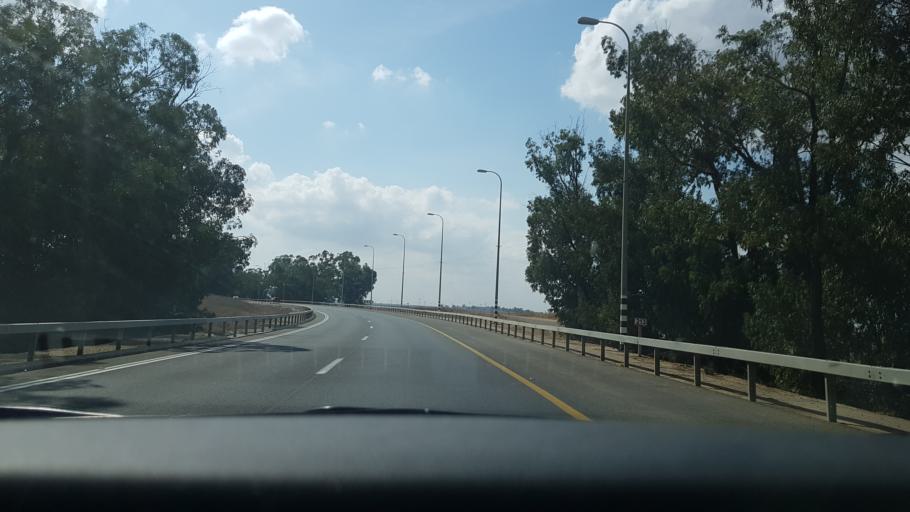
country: IL
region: Southern District
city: Lehavim
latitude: 31.4797
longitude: 34.7747
